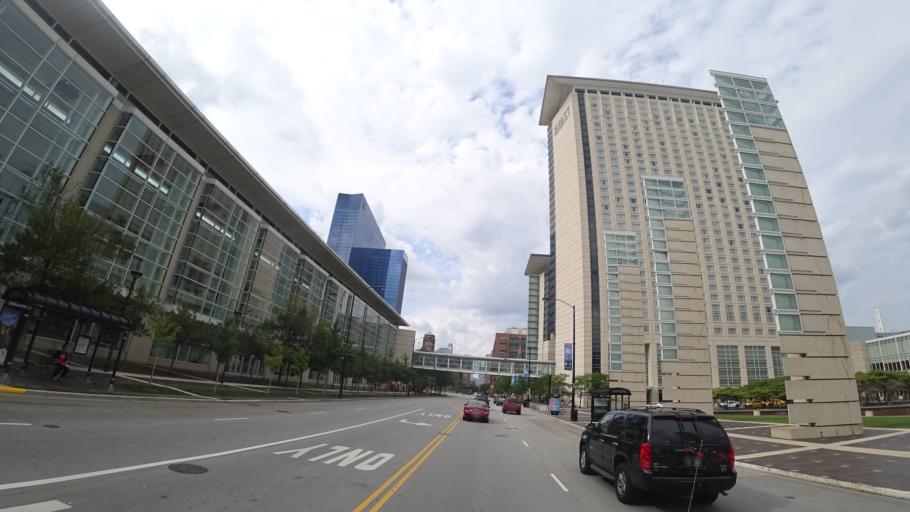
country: US
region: Illinois
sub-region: Cook County
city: Chicago
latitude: 41.8509
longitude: -87.6189
